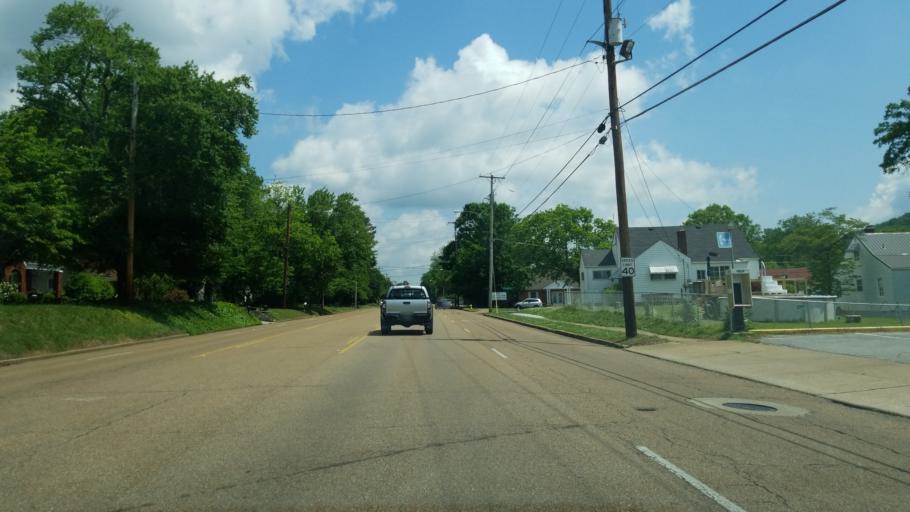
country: US
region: Tennessee
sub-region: Hamilton County
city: Red Bank
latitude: 35.1292
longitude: -85.2835
